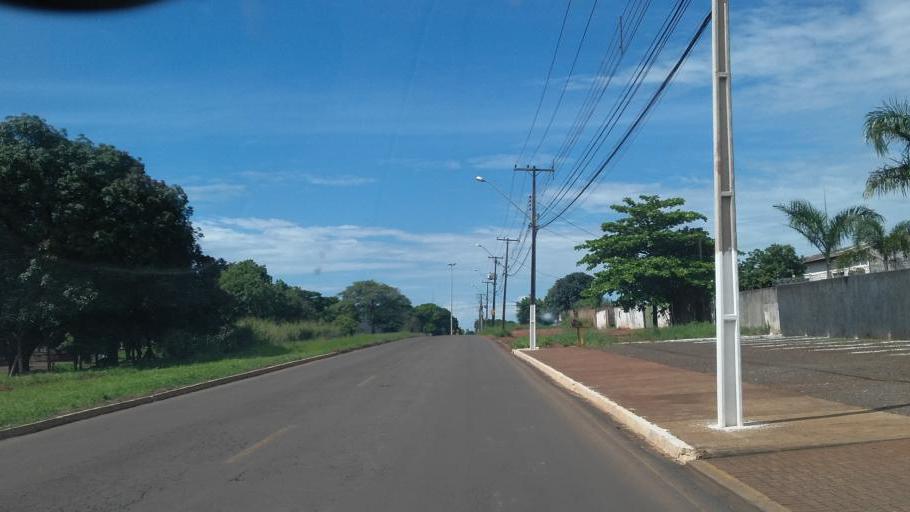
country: BR
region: Parana
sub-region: Londrina
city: Londrina
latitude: -23.2862
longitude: -51.2099
